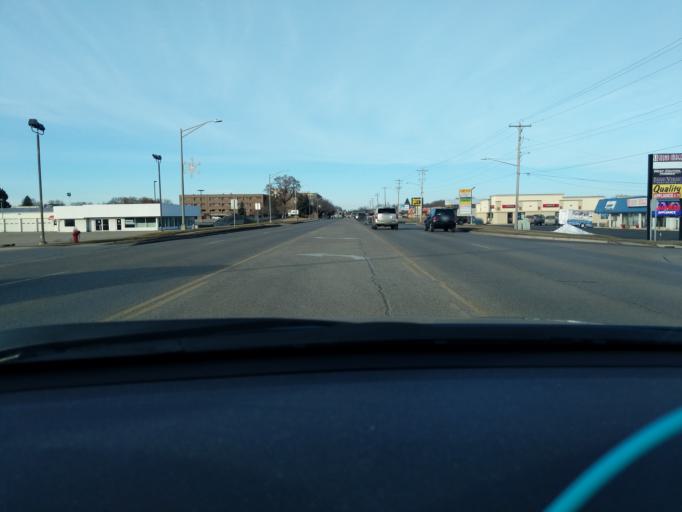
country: US
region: Minnesota
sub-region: Kandiyohi County
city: Willmar
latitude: 45.1067
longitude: -95.0427
